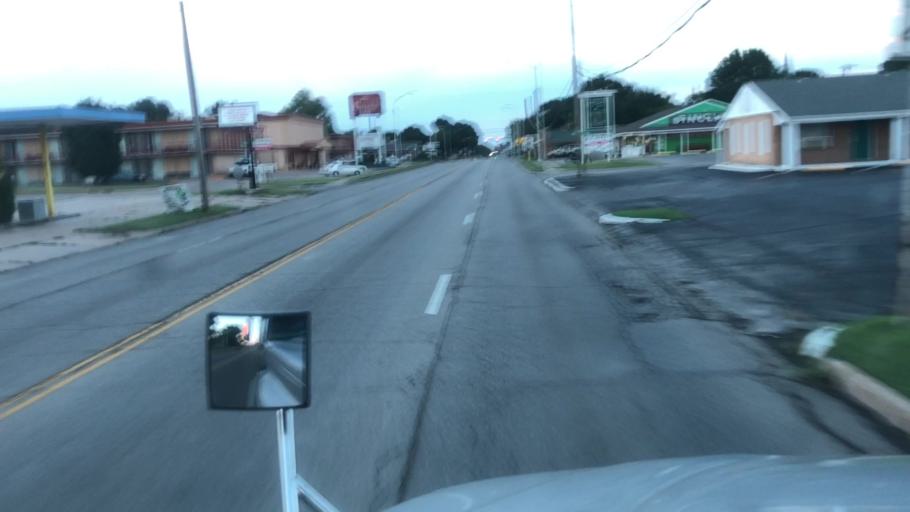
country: US
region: Oklahoma
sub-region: Kay County
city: Ponca City
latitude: 36.7007
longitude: -97.0672
